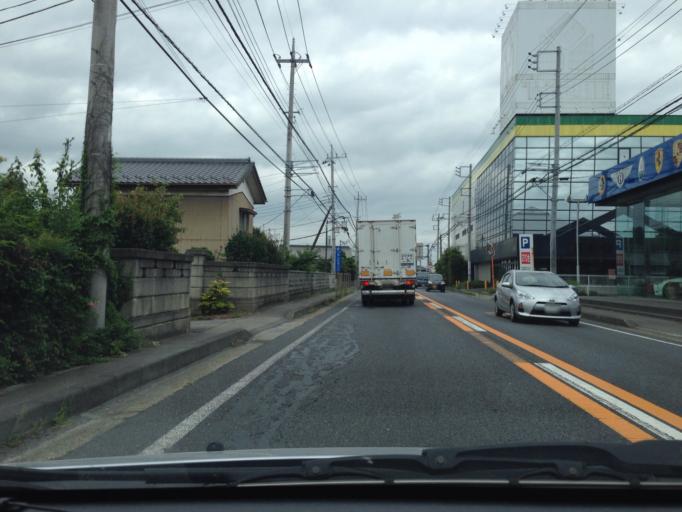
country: JP
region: Ibaraki
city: Ushiku
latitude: 35.9930
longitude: 140.1469
